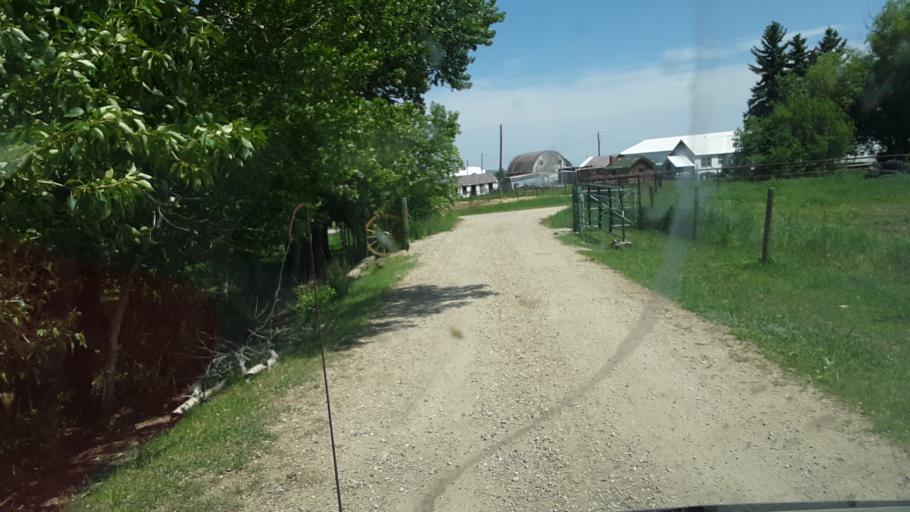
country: US
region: Montana
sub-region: Carbon County
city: Red Lodge
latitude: 45.3617
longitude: -109.1864
